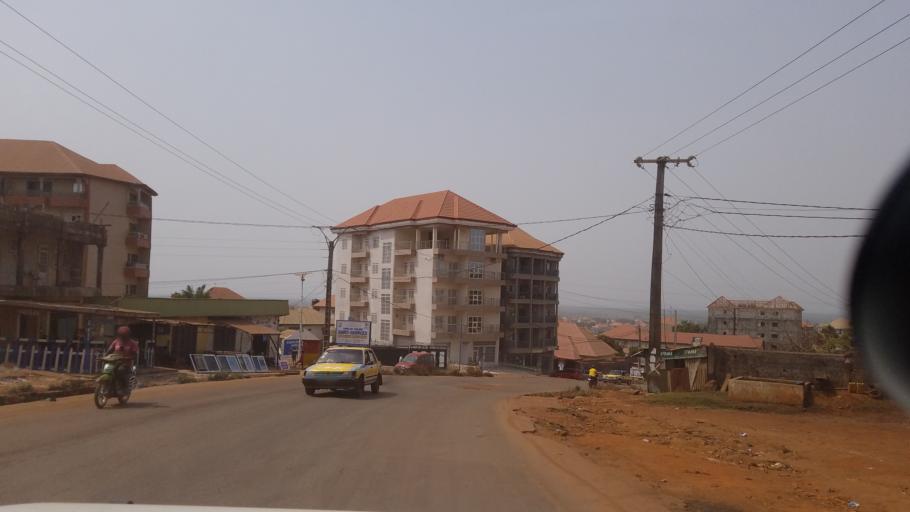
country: GN
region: Kindia
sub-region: Prefecture de Dubreka
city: Dubreka
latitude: 9.6721
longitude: -13.5633
